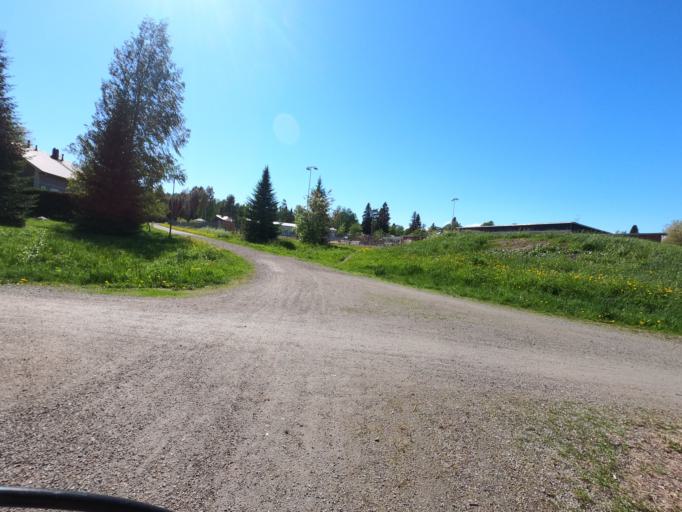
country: FI
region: North Karelia
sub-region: Joensuu
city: Joensuu
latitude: 62.5939
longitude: 29.7955
